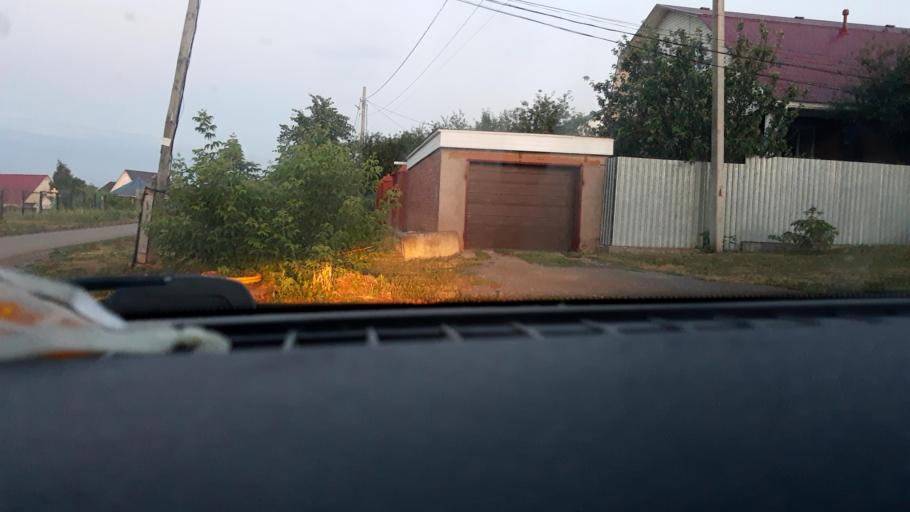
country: RU
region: Bashkortostan
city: Avdon
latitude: 54.6194
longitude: 55.6426
